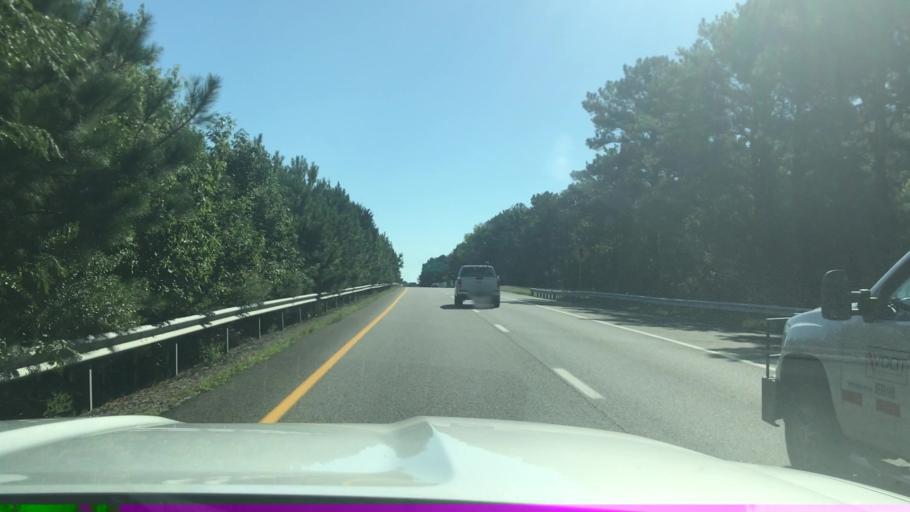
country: US
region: Virginia
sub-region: Henrico County
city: Sandston
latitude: 37.5299
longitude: -77.3296
